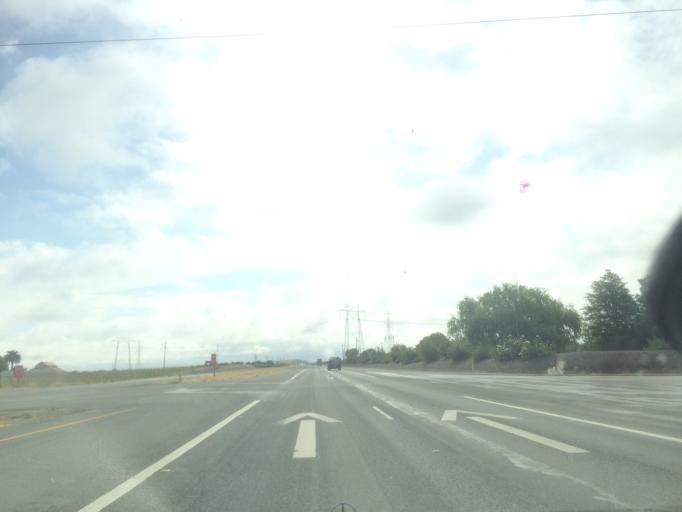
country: US
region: California
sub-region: San Luis Obispo County
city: Paso Robles
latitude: 35.6593
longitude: -120.5794
